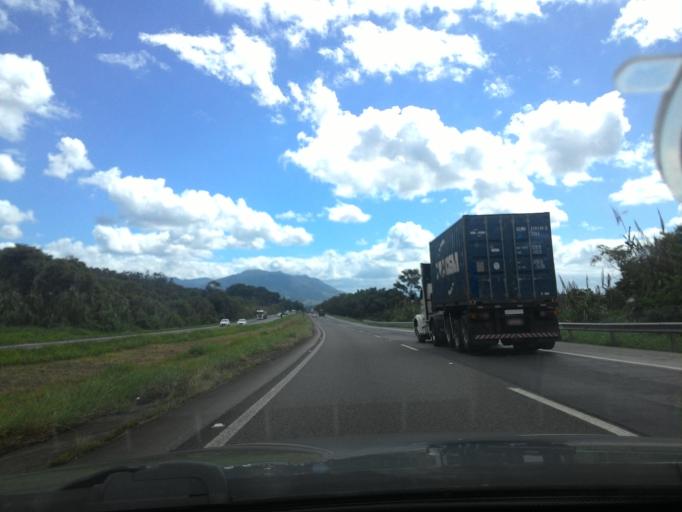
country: BR
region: Sao Paulo
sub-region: Jacupiranga
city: Jacupiranga
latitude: -24.7174
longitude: -48.0371
